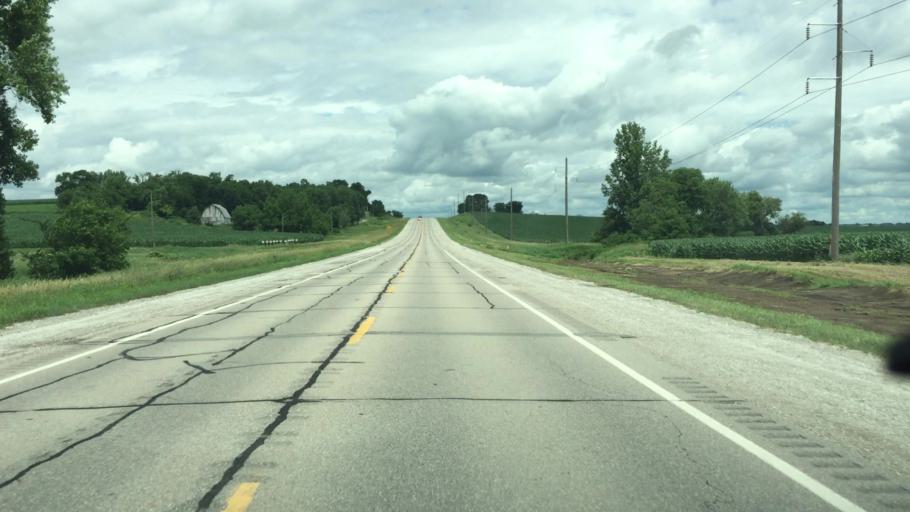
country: US
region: Iowa
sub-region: Jasper County
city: Monroe
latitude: 41.5862
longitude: -93.0971
